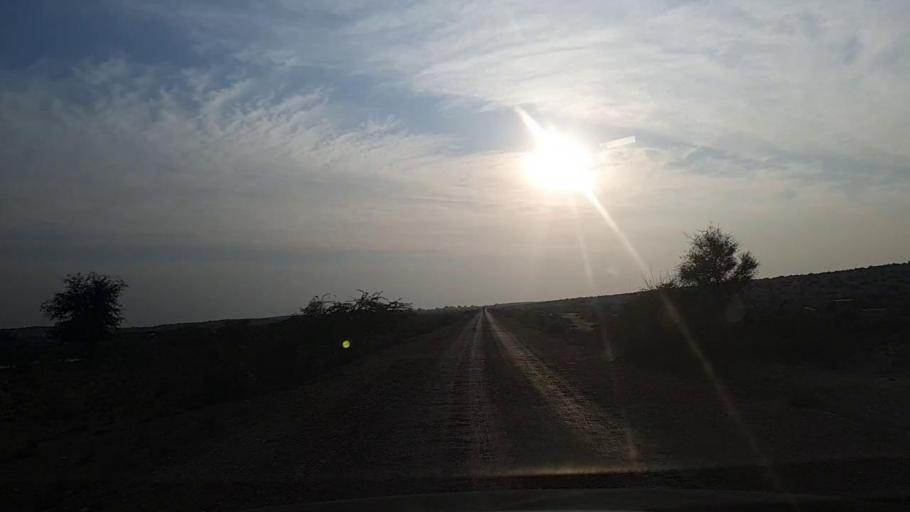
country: PK
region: Sindh
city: Jam Sahib
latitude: 26.4178
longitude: 68.5203
